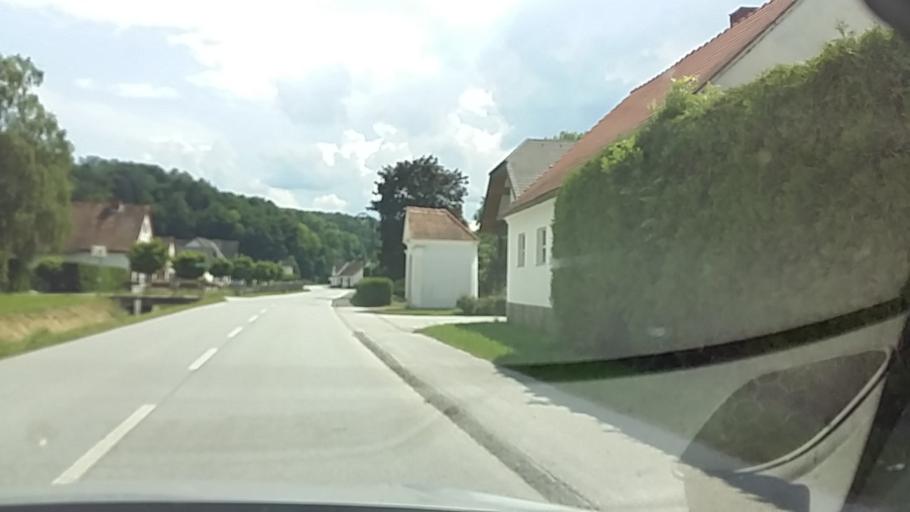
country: AT
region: Styria
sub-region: Politischer Bezirk Suedoststeiermark
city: Breitenfeld an der Rittschein
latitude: 47.0342
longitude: 15.9601
